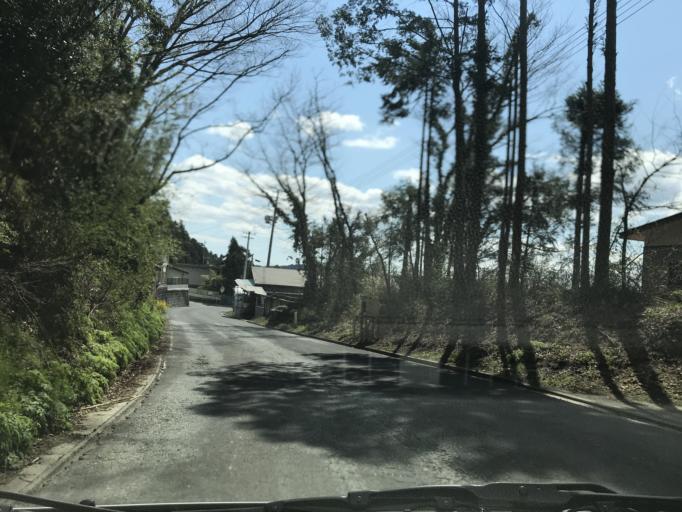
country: JP
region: Miyagi
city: Wakuya
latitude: 38.6460
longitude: 141.2472
